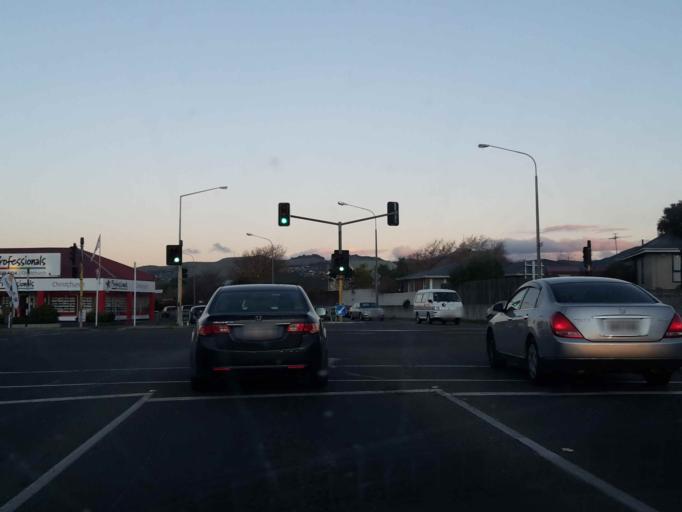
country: NZ
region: Canterbury
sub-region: Christchurch City
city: Christchurch
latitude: -43.5546
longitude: 172.5925
